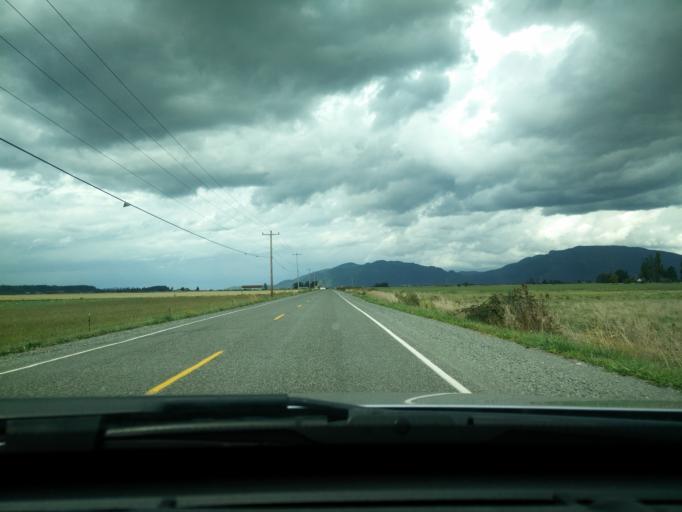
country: US
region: Washington
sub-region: Skagit County
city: Anacortes
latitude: 48.5325
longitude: -122.4719
